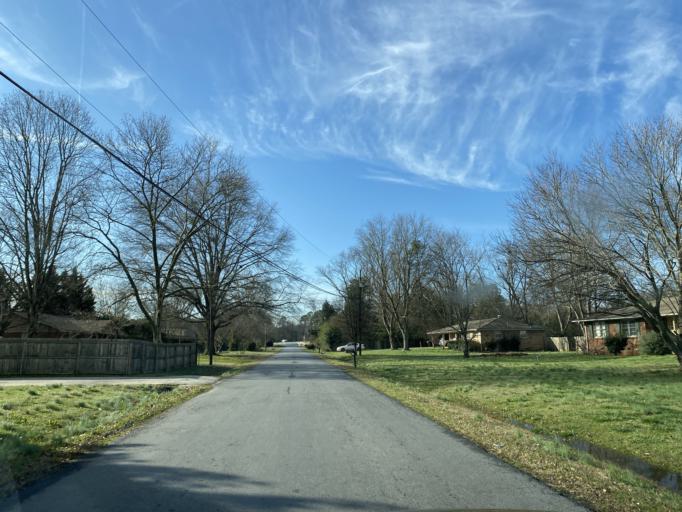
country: US
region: Georgia
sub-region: Bartow County
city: Cartersville
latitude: 34.2114
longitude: -84.8228
